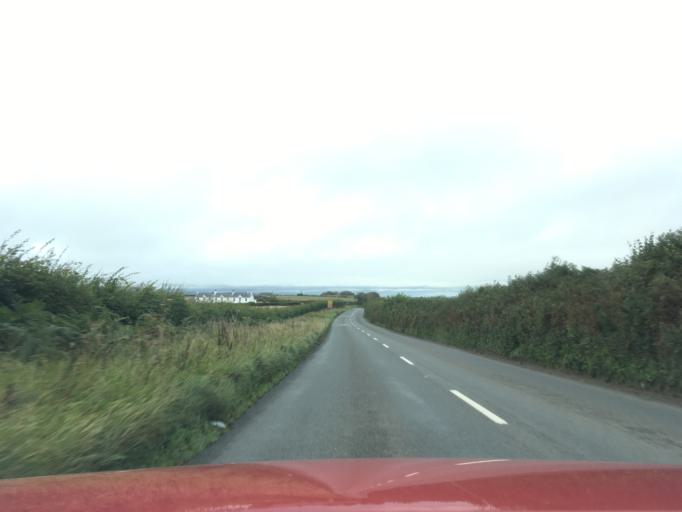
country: GB
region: England
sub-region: Devon
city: Kingsbridge
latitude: 50.2895
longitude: -3.8141
